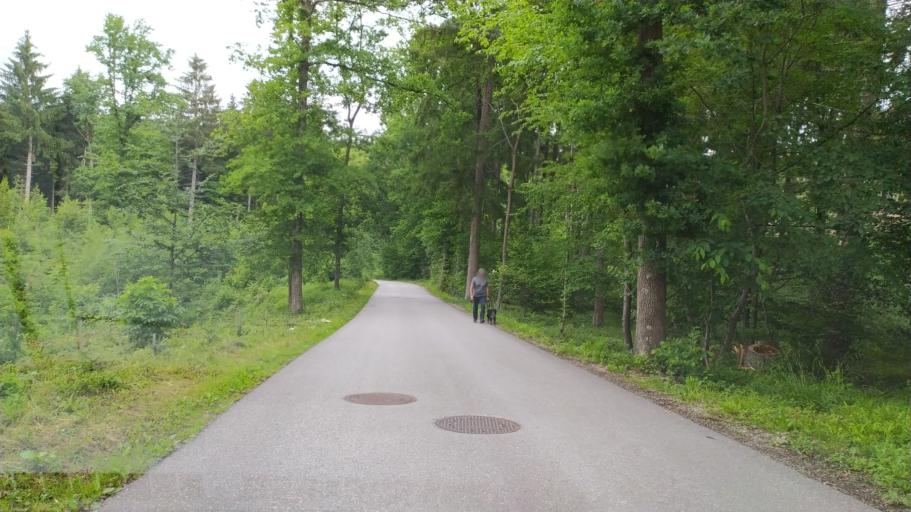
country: AT
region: Upper Austria
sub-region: Politischer Bezirk Perg
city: Perg
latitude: 48.2570
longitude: 14.6618
